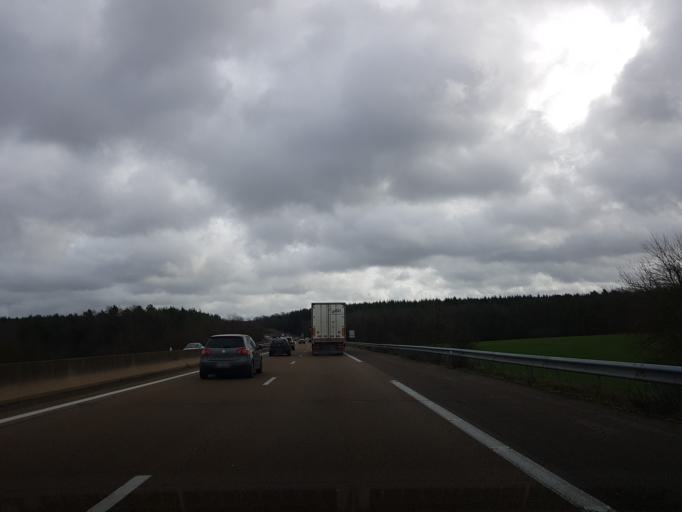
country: FR
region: Champagne-Ardenne
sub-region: Departement de la Haute-Marne
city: Chamarandes-Choignes
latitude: 47.9572
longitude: 5.1556
